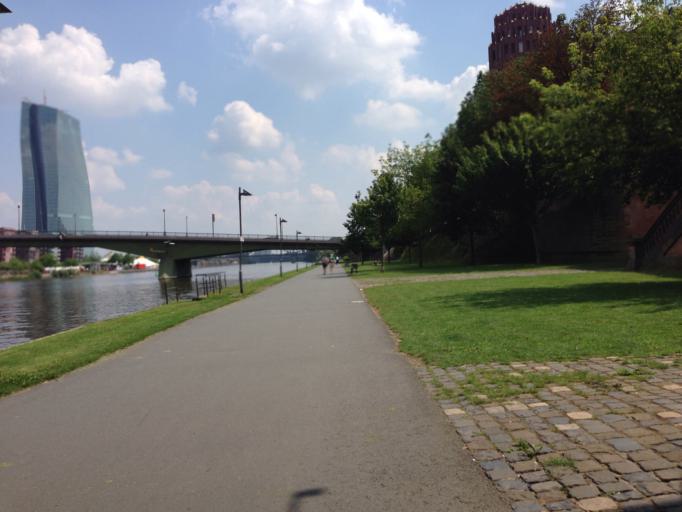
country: DE
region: Hesse
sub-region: Regierungsbezirk Darmstadt
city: Frankfurt am Main
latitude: 50.1072
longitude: 8.6926
